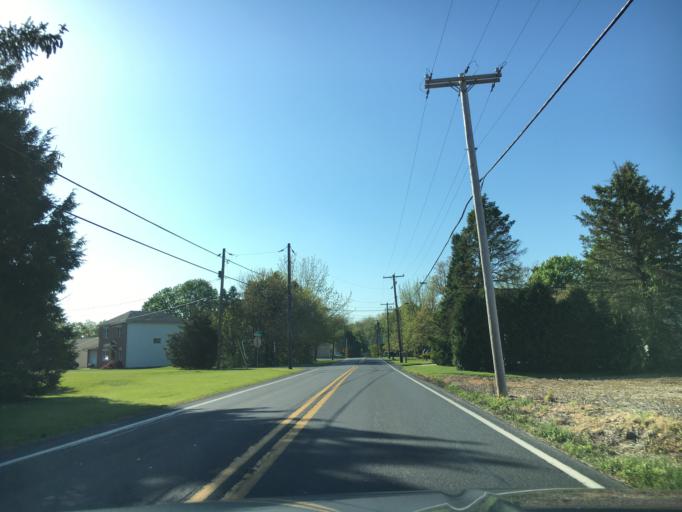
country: US
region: Pennsylvania
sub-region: Northampton County
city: North Catasauqua
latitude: 40.6766
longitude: -75.4348
